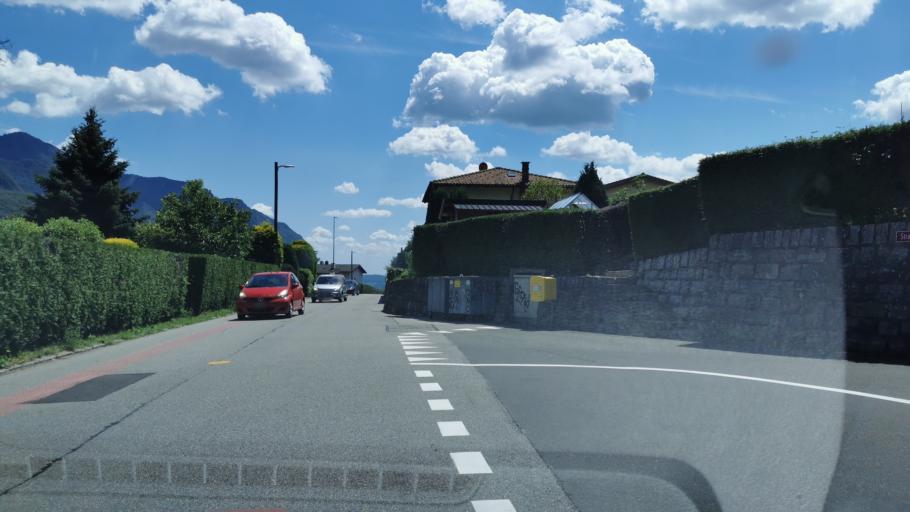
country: IT
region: Lombardy
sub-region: Provincia di Como
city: Campione
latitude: 45.9574
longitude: 8.9848
